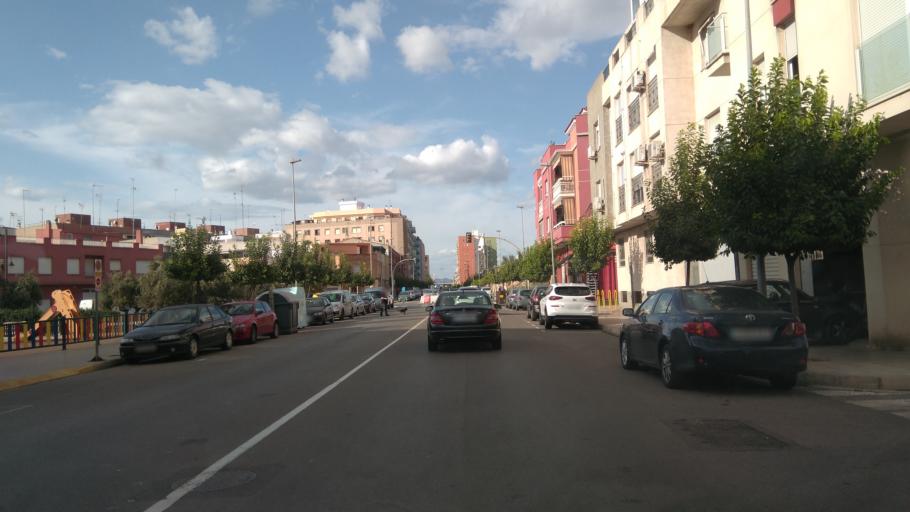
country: ES
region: Valencia
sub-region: Provincia de Valencia
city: Alzira
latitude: 39.1536
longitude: -0.4262
